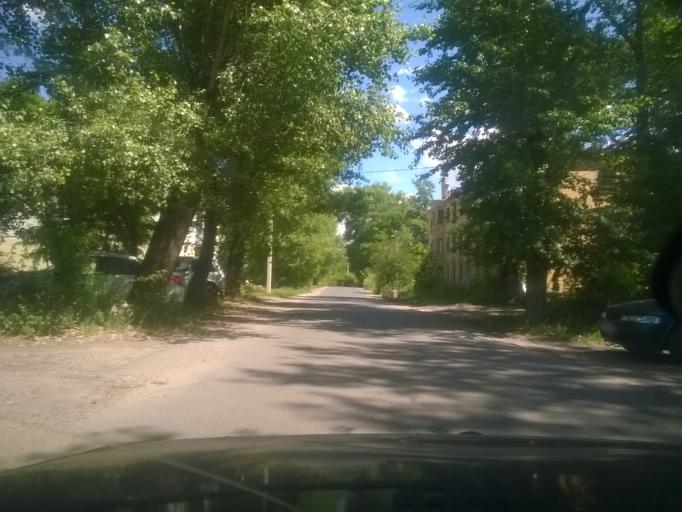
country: RU
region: Kursk
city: Voroshnevo
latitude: 51.6657
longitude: 36.1058
